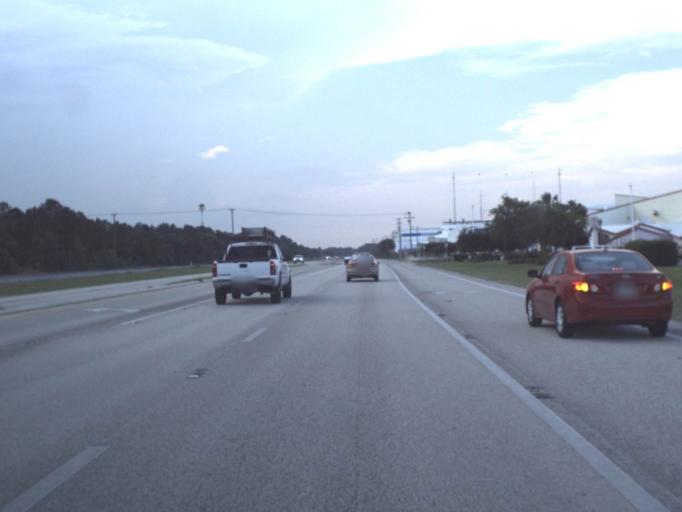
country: US
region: Florida
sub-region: Saint Johns County
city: Villano Beach
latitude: 29.9529
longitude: -81.3426
